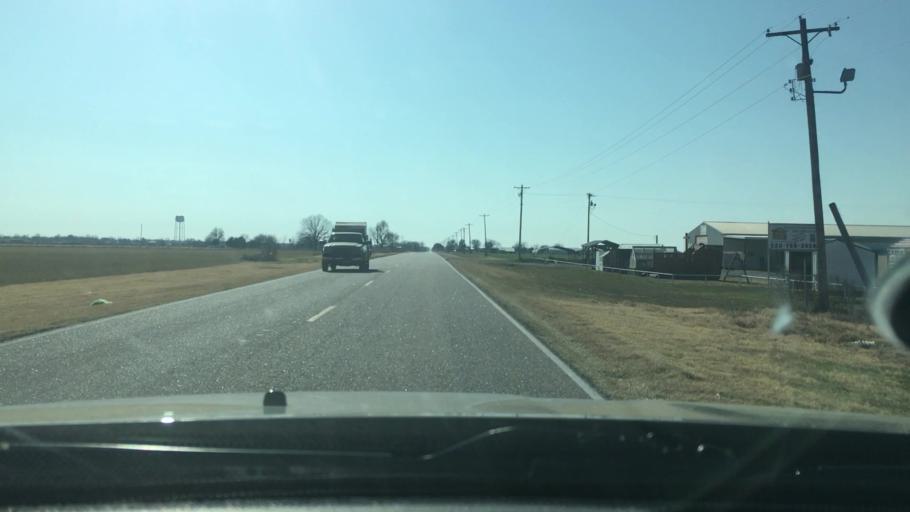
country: US
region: Oklahoma
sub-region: Garvin County
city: Stratford
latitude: 34.8196
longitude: -96.9677
